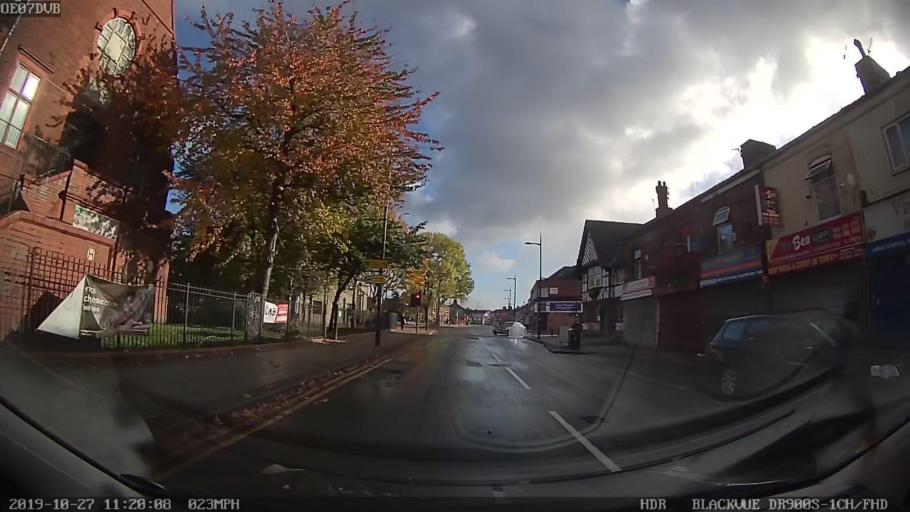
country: GB
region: England
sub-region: Manchester
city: Blackley
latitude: 53.5140
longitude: -2.1972
